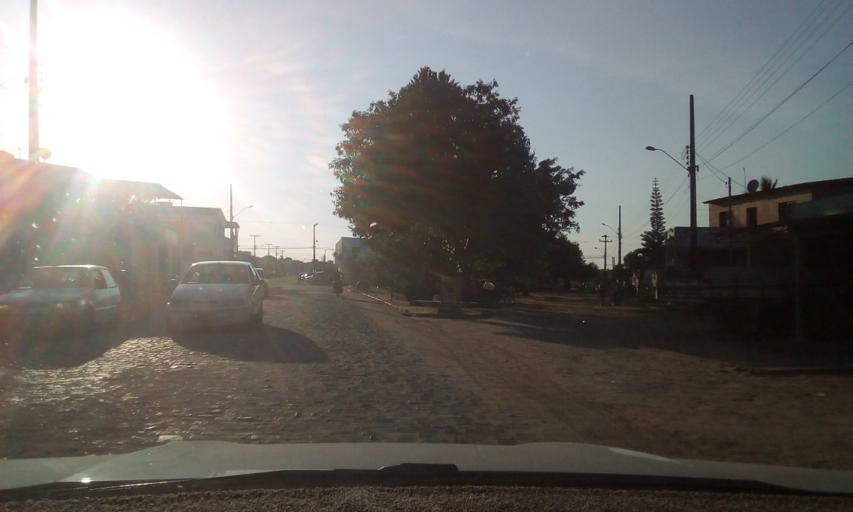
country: BR
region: Paraiba
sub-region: Bayeux
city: Bayeux
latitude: -7.1762
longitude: -34.9317
